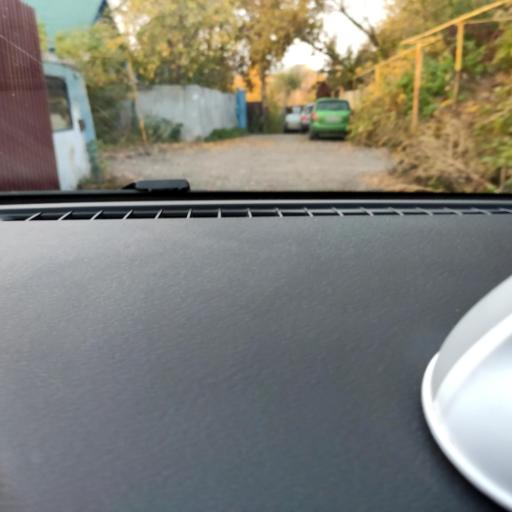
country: RU
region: Samara
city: Samara
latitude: 53.1821
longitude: 50.1233
